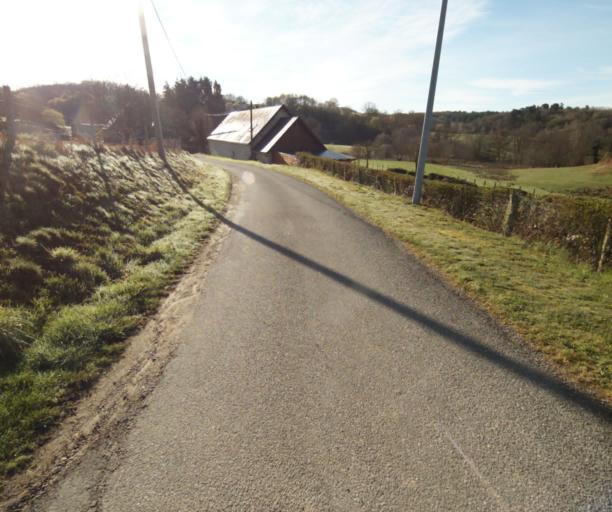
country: FR
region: Limousin
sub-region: Departement de la Correze
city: Correze
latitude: 45.2775
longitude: 1.8722
